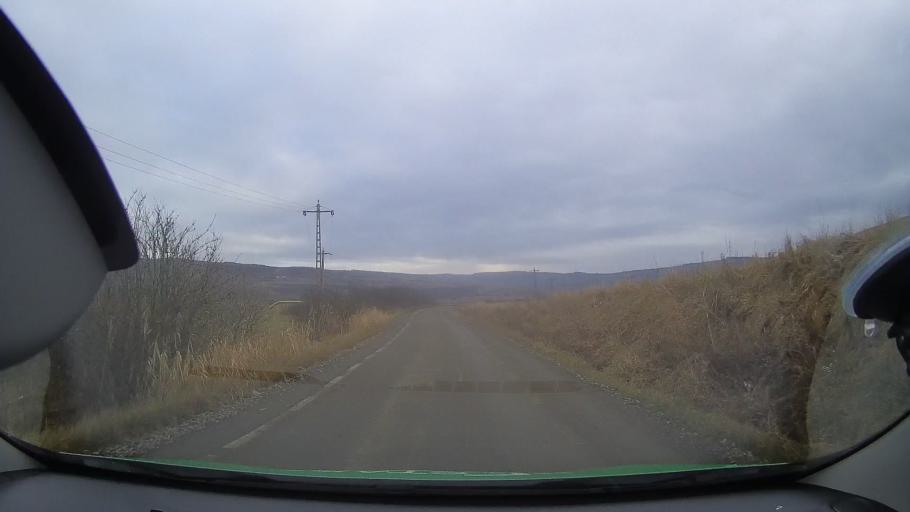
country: RO
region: Mures
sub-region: Comuna Atintis
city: Atintis
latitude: 46.4057
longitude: 24.0869
